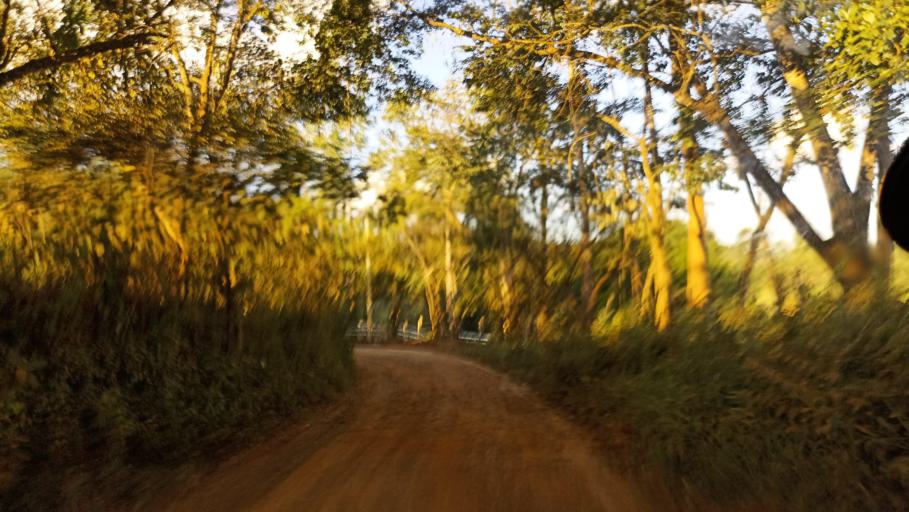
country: BR
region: Minas Gerais
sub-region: Sao Joao Del Rei
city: Sao Joao del Rei
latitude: -21.1833
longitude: -44.3457
